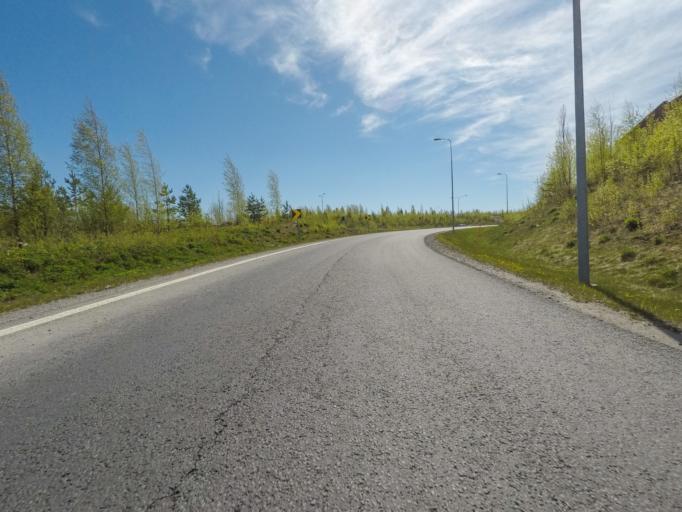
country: FI
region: Pirkanmaa
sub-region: Tampere
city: Tampere
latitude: 61.4510
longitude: 23.7647
